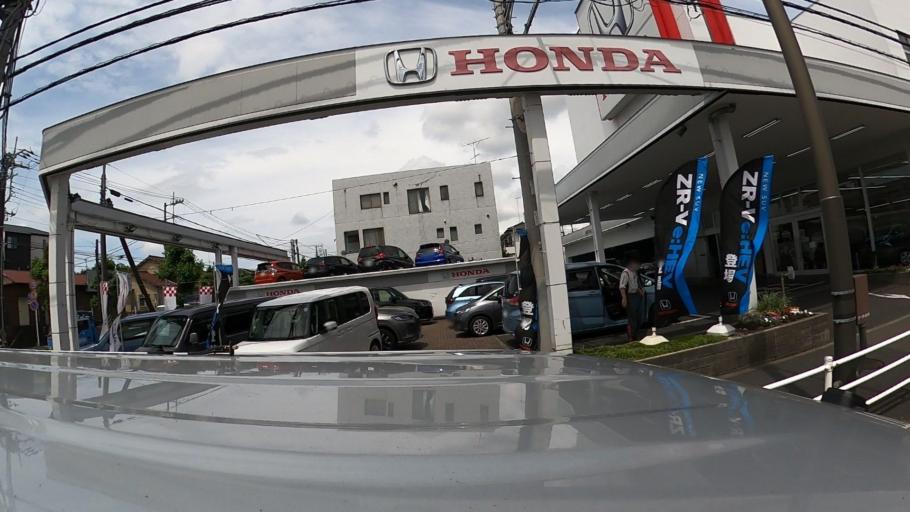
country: JP
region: Kanagawa
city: Fujisawa
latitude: 35.4027
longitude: 139.4698
